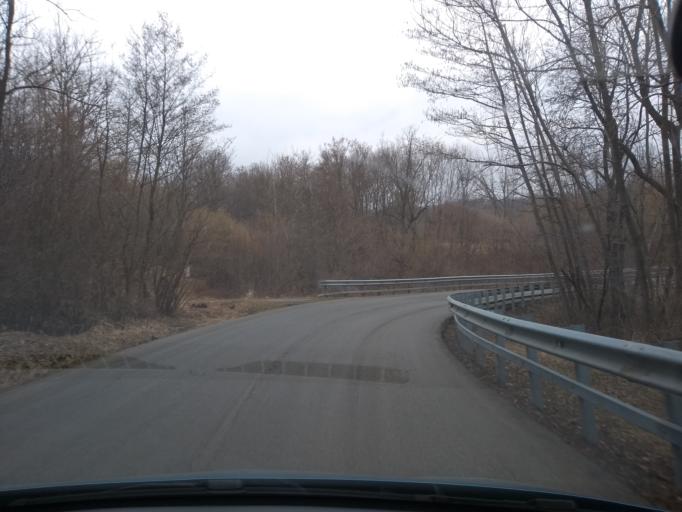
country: IT
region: Piedmont
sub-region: Provincia di Biella
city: Torrazzo
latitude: 45.4861
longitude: 7.9703
